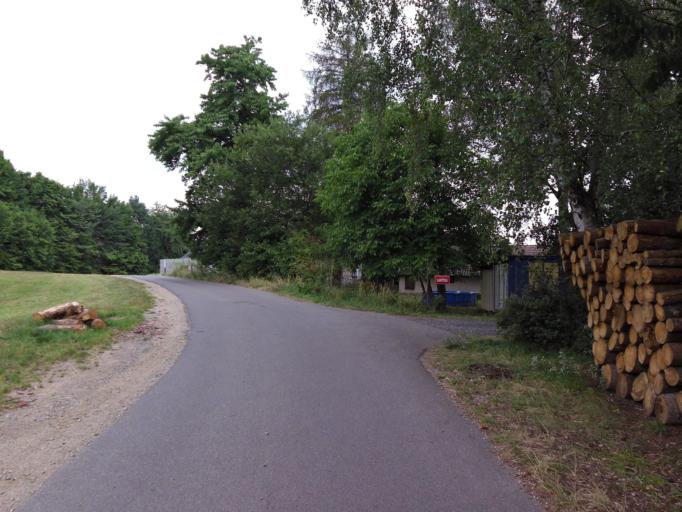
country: CZ
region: Central Bohemia
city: Kamenice
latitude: 49.8899
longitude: 14.6141
